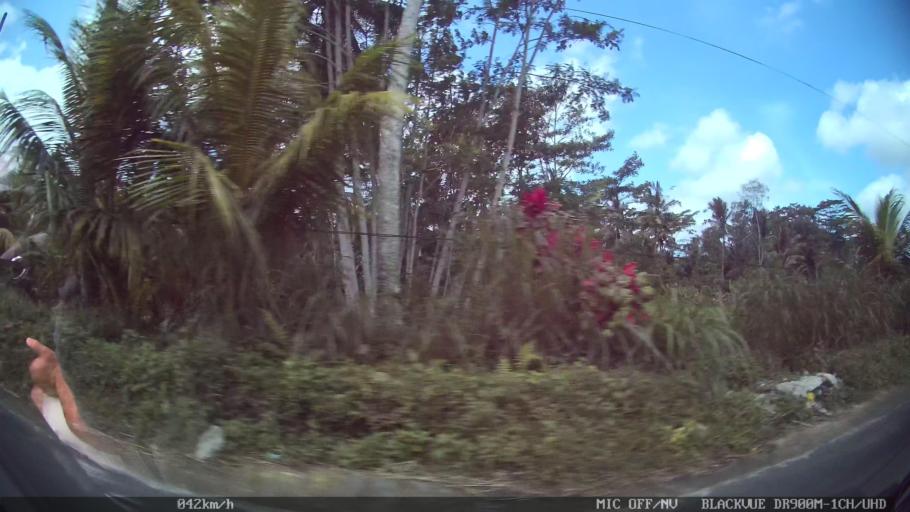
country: ID
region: Bali
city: Banjar Bebalang
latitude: -8.4736
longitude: 115.3425
